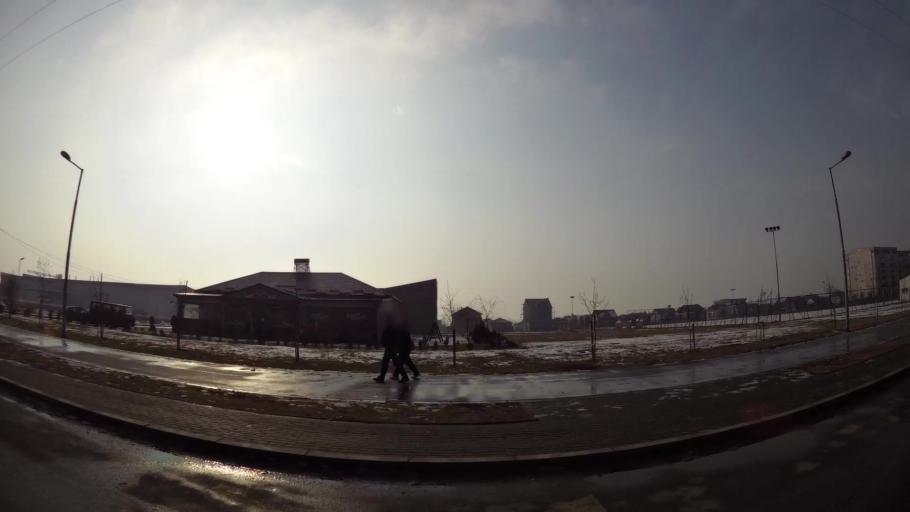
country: MK
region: Ilinden
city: Marino
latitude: 41.9867
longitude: 21.5889
